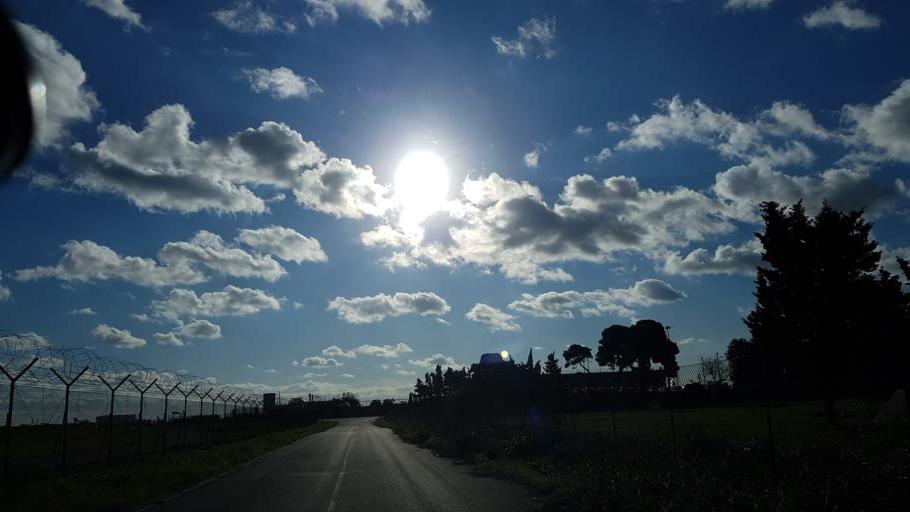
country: IT
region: Apulia
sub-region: Provincia di Brindisi
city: Materdomini
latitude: 40.6612
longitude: 17.9405
